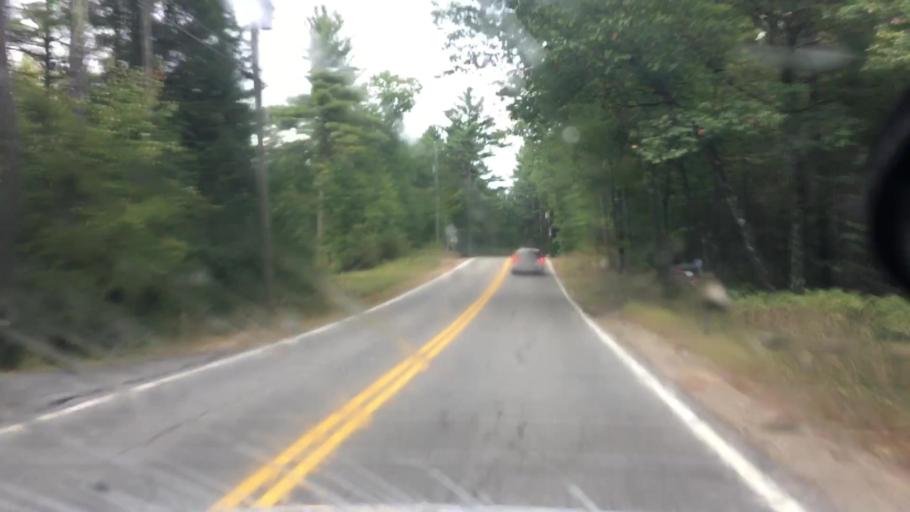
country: US
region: Maine
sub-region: York County
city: Parsonsfield
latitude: 43.6624
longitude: -70.9912
